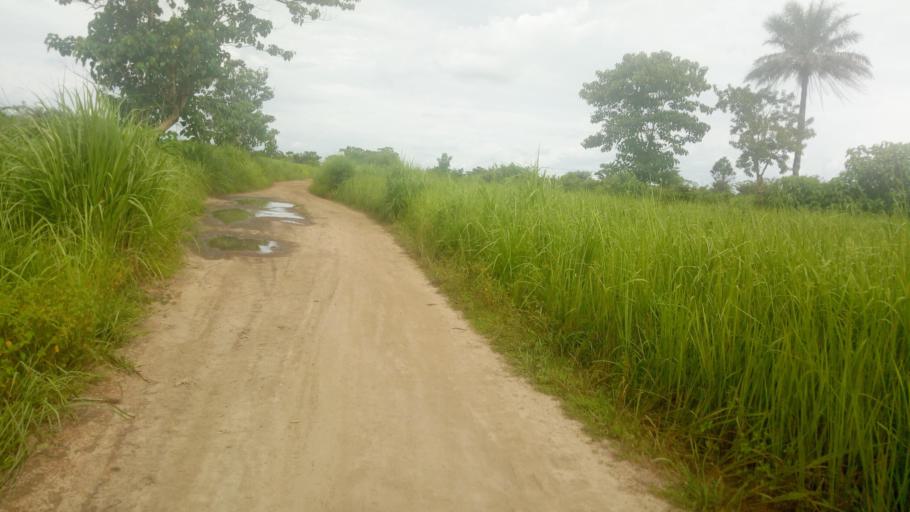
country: SL
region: Northern Province
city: Magburaka
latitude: 8.6729
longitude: -12.0318
